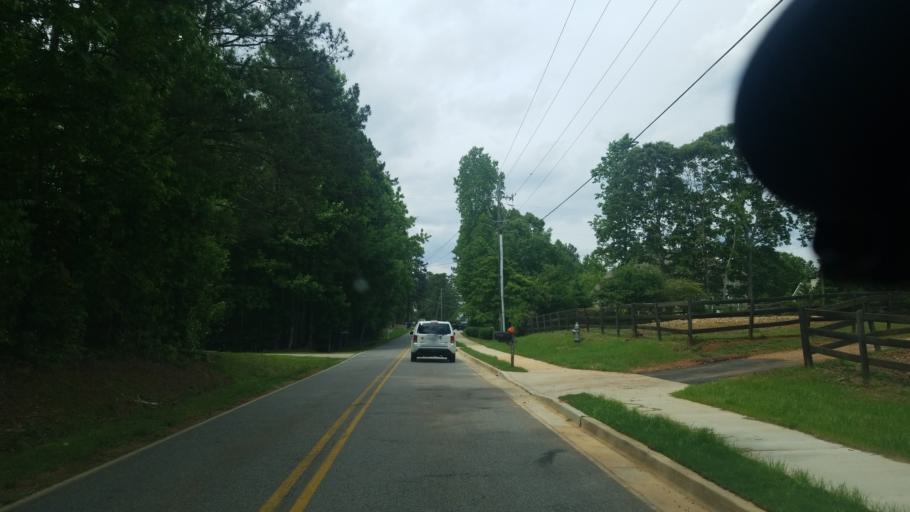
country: US
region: Georgia
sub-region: Forsyth County
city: Cumming
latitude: 34.1577
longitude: -84.0997
